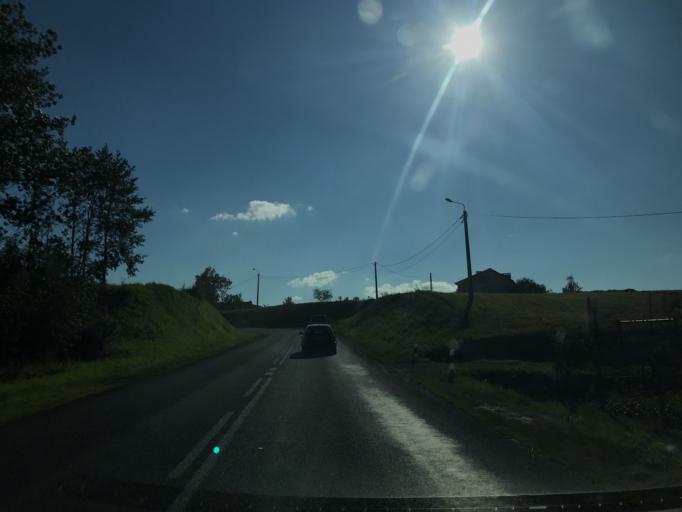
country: PL
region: Kujawsko-Pomorskie
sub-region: Powiat wloclawski
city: Brzesc Kujawski
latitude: 52.5976
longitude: 18.8949
